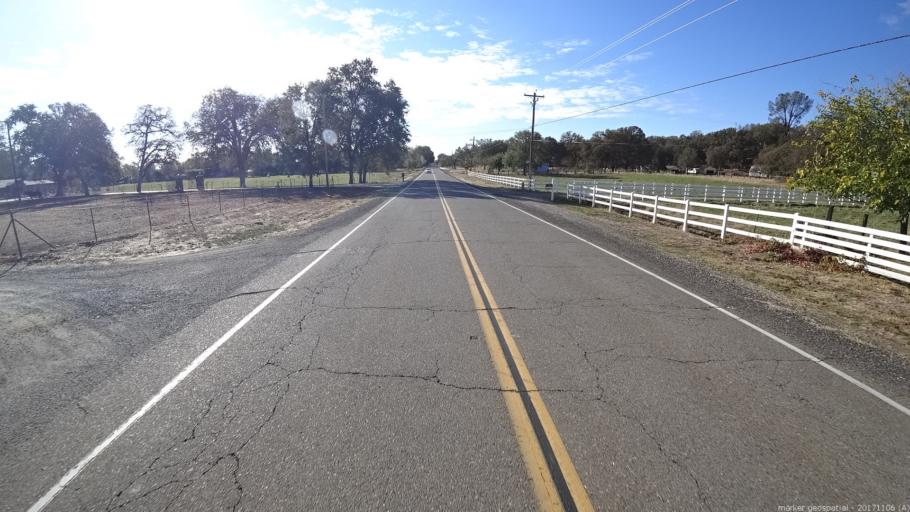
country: US
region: California
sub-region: Shasta County
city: Palo Cedro
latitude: 40.5222
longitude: -122.2385
